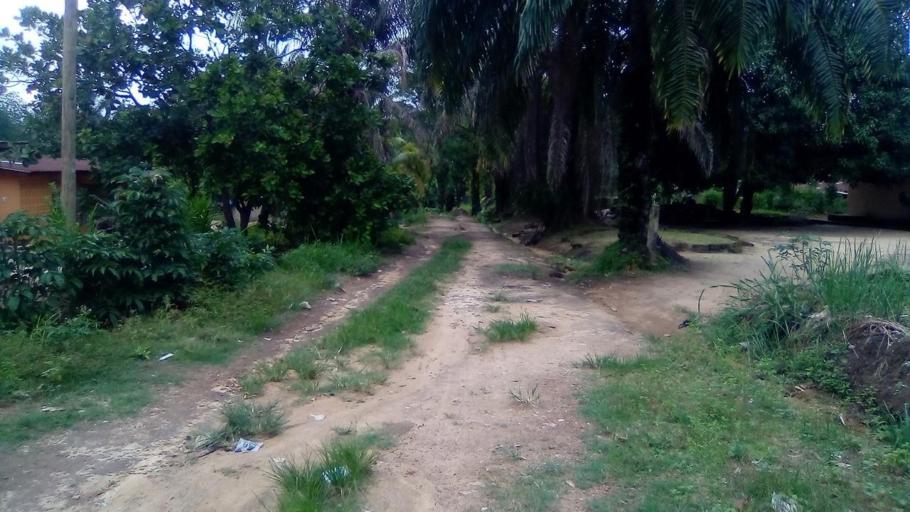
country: SL
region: Southern Province
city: Bo
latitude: 7.9501
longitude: -11.7507
